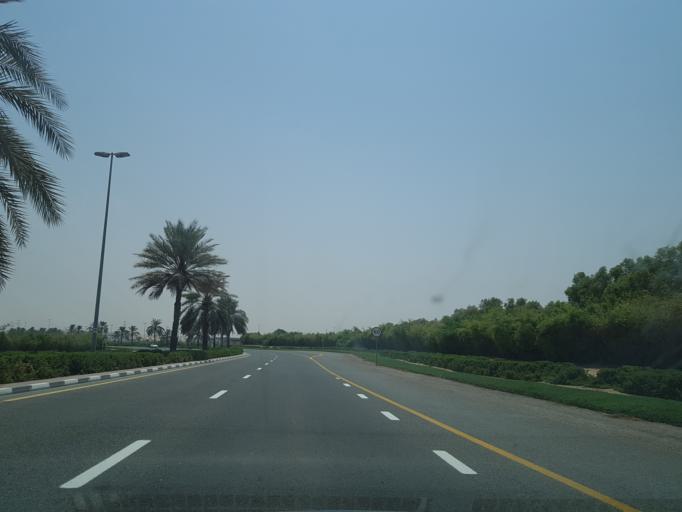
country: AE
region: Ash Shariqah
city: Sharjah
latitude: 25.1113
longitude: 55.3951
